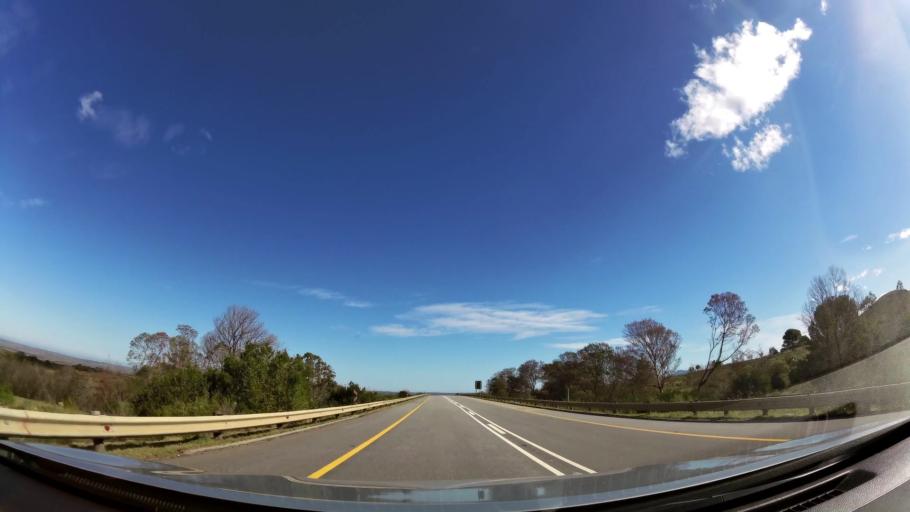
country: ZA
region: Eastern Cape
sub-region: Cacadu District Municipality
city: Kruisfontein
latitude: -33.9974
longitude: 24.6882
